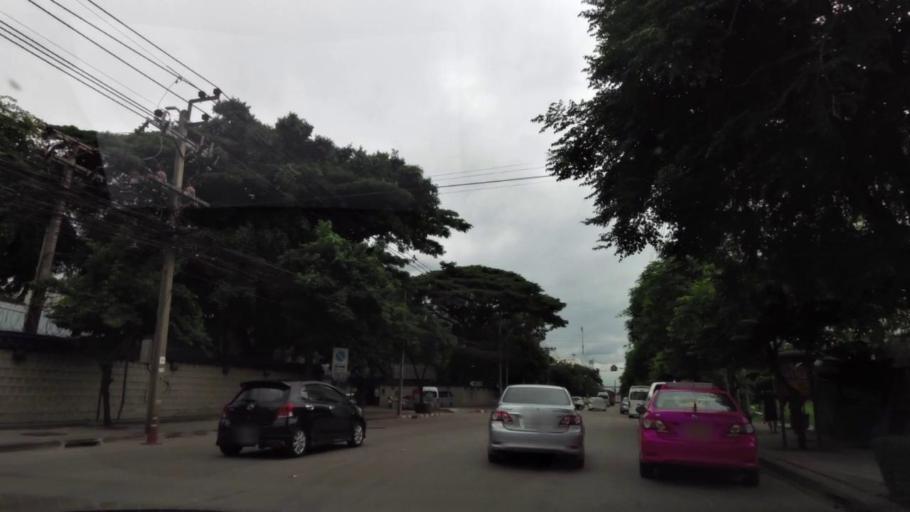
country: TH
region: Bangkok
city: Huai Khwang
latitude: 13.7673
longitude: 100.5776
